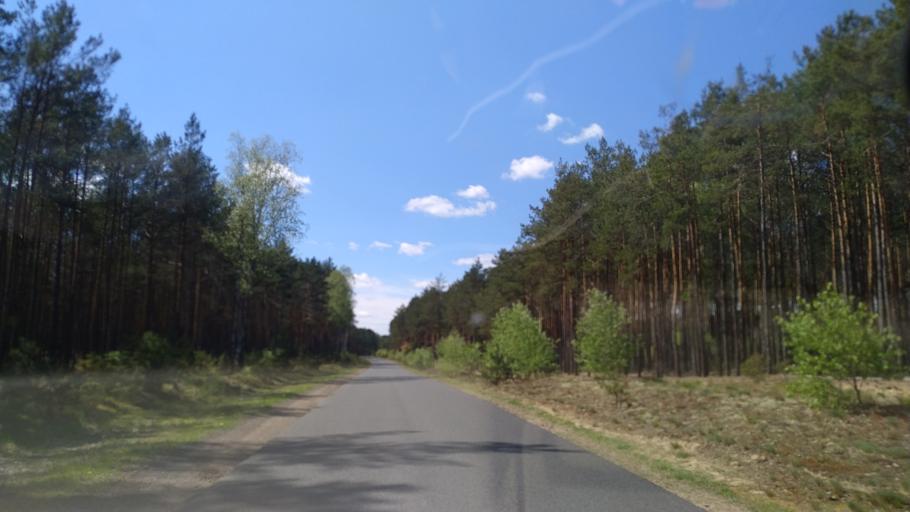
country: PL
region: Greater Poland Voivodeship
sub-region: Powiat zlotowski
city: Tarnowka
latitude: 53.2717
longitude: 16.8596
